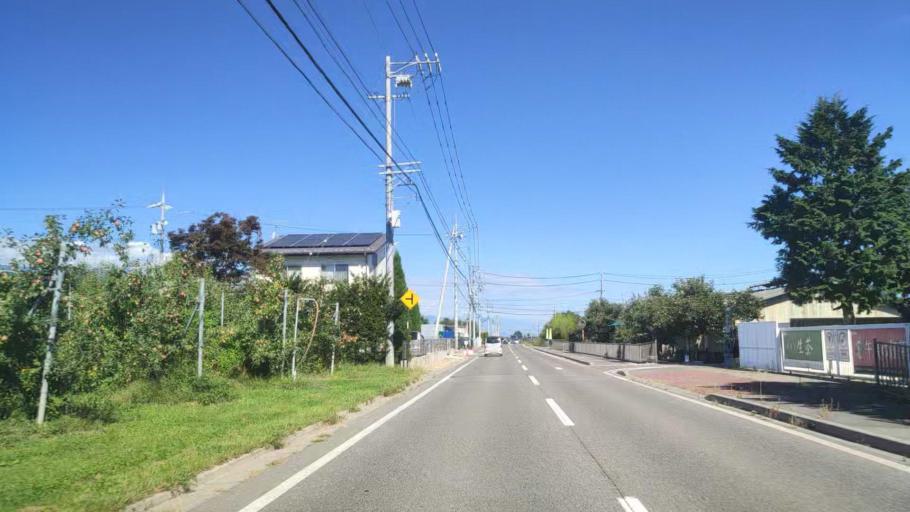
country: JP
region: Nagano
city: Matsumoto
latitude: 36.1744
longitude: 137.9141
